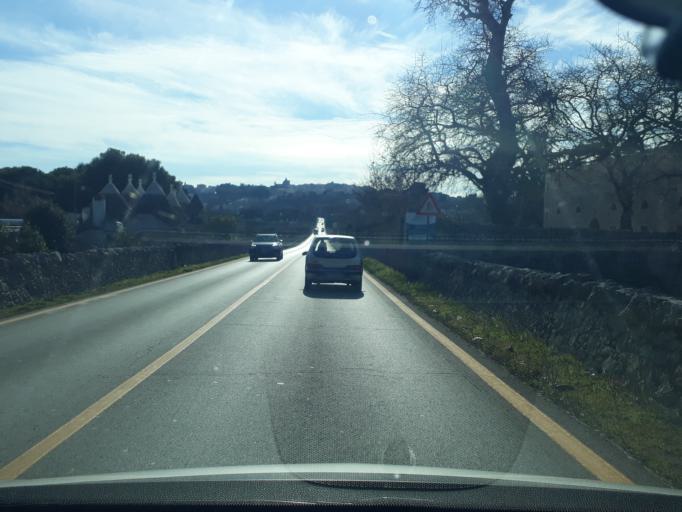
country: IT
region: Apulia
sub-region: Provincia di Taranto
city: Martina Franca
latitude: 40.7181
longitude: 17.3327
